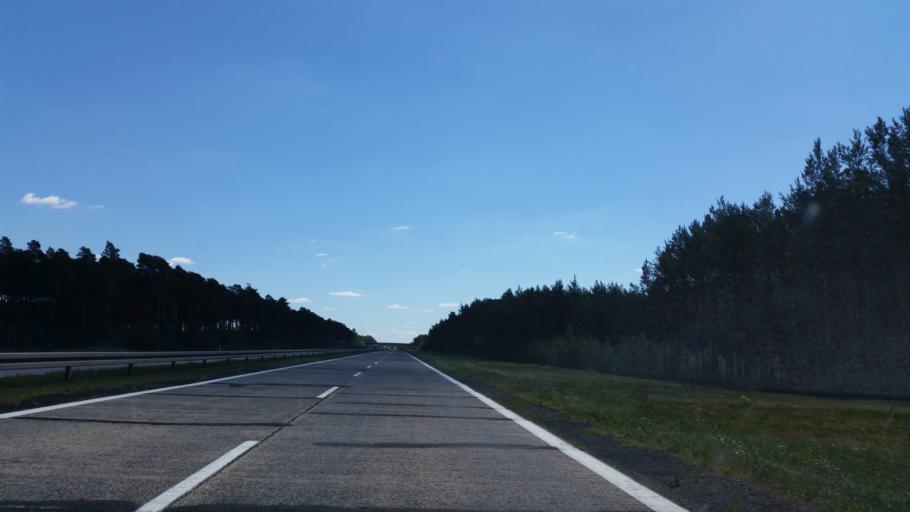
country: PL
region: Lower Silesian Voivodeship
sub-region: Powiat boleslawiecki
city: Boleslawiec
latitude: 51.3807
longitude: 15.5499
